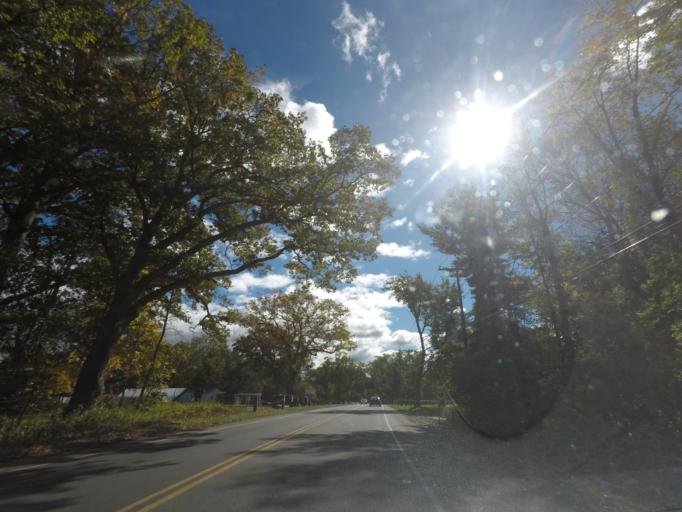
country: US
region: New York
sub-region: Albany County
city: Watervliet
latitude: 42.7261
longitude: -73.7274
